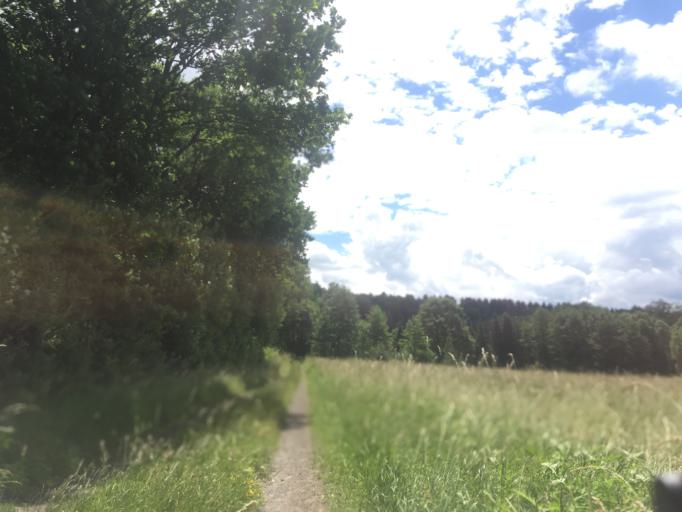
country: DE
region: Rheinland-Pfalz
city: Girod
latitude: 50.4501
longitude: 7.9316
